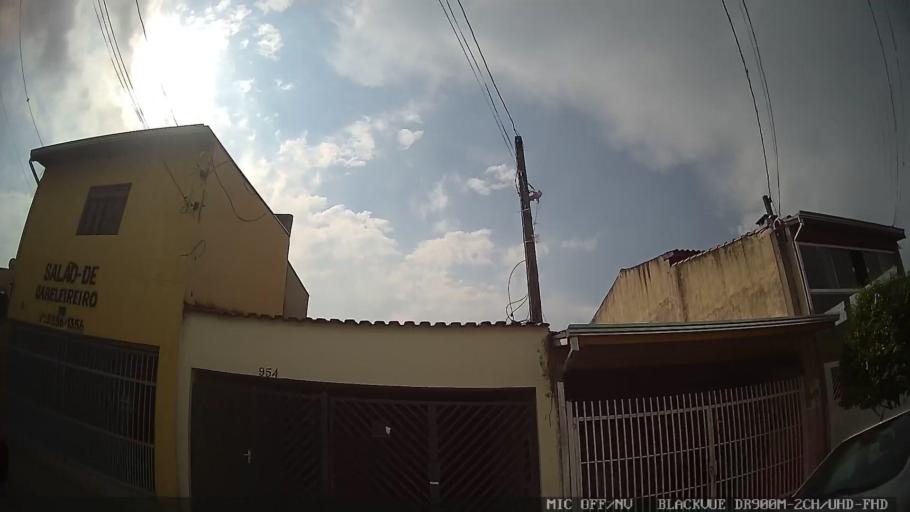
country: BR
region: Sao Paulo
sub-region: Indaiatuba
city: Indaiatuba
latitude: -23.1206
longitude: -47.2432
